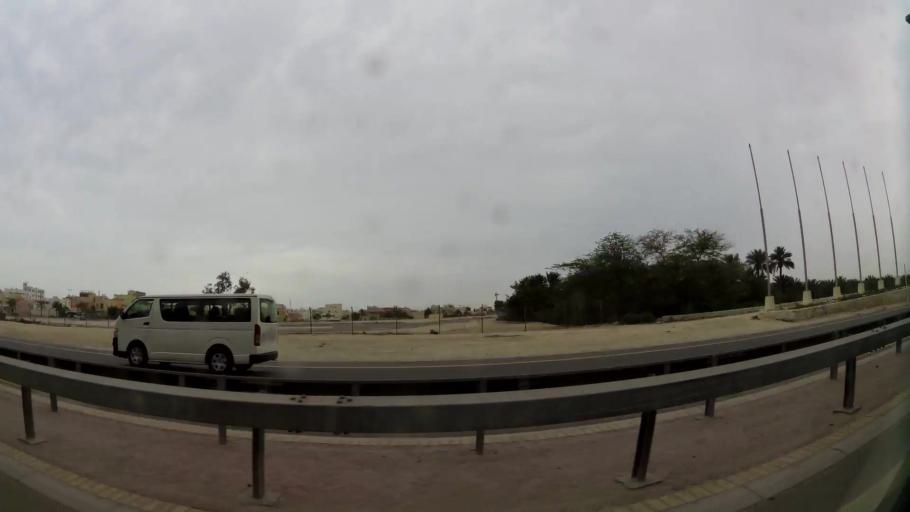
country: BH
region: Northern
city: Ar Rifa'
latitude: 26.1186
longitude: 50.5370
